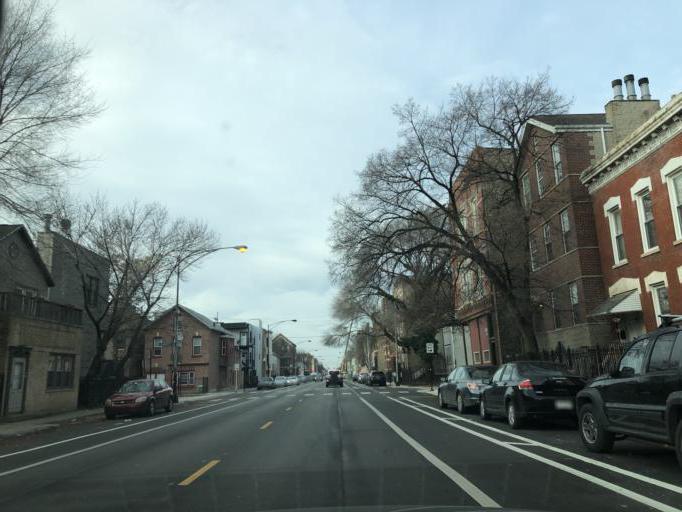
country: US
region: Illinois
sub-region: Cook County
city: Chicago
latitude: 41.8996
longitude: -87.6730
